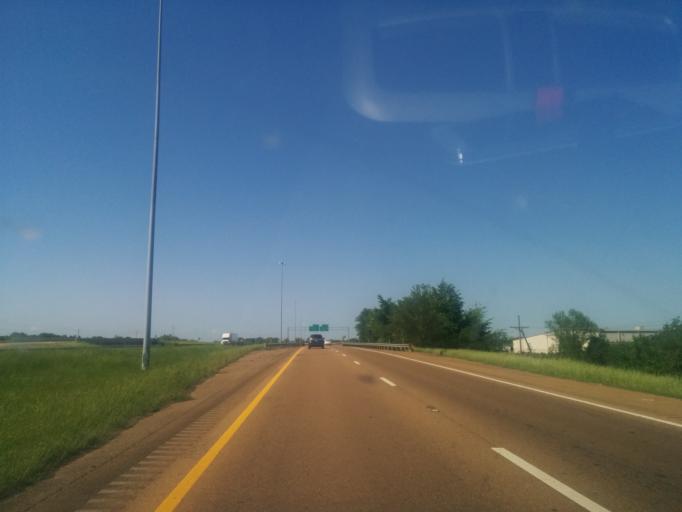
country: US
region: Mississippi
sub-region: Madison County
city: Madison
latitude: 32.5301
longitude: -90.0952
